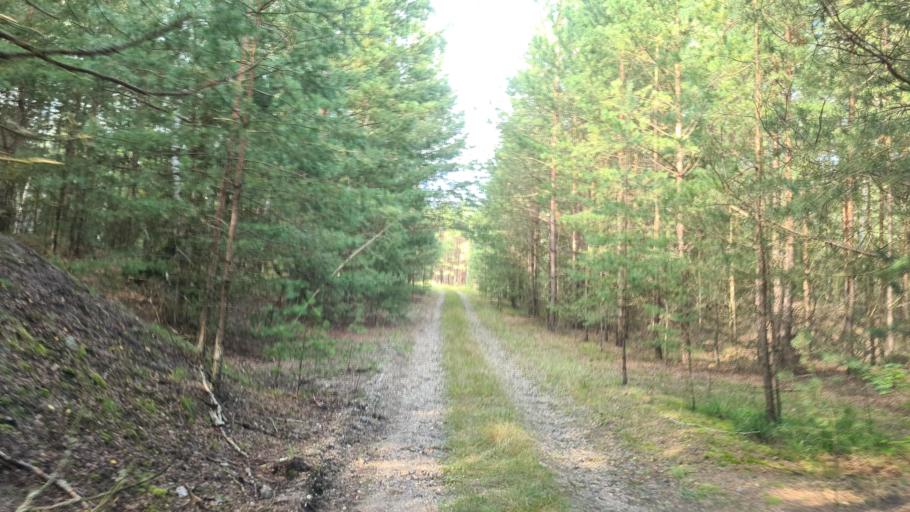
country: DE
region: Brandenburg
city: Schonborn
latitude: 51.6073
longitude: 13.4725
